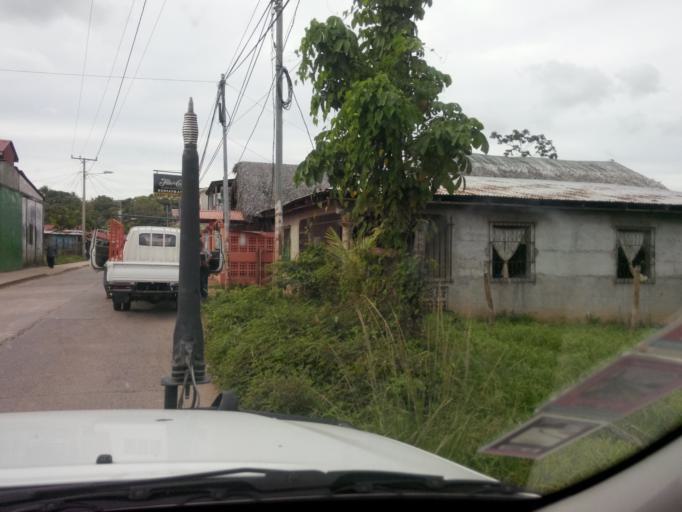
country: NI
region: Atlantico Sur
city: Bluefields
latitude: 12.0256
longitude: -83.7670
